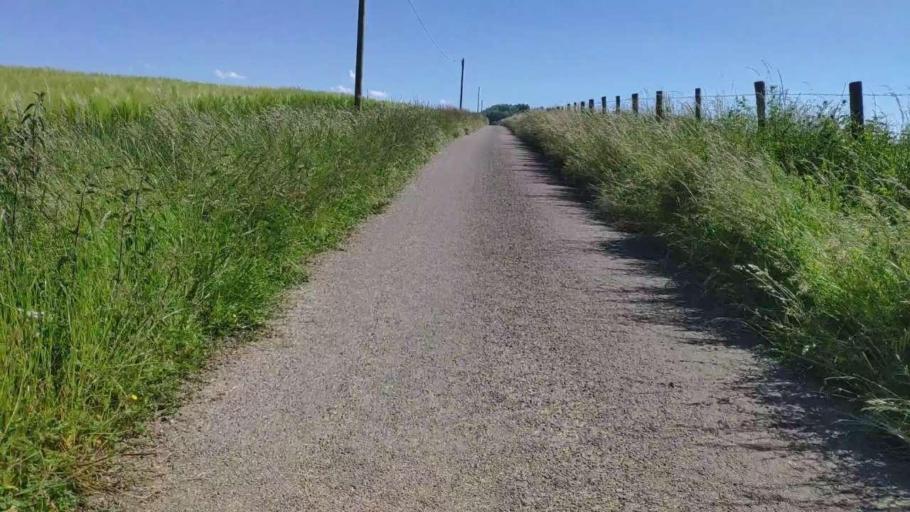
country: FR
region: Franche-Comte
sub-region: Departement du Jura
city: Perrigny
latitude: 46.7372
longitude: 5.5837
